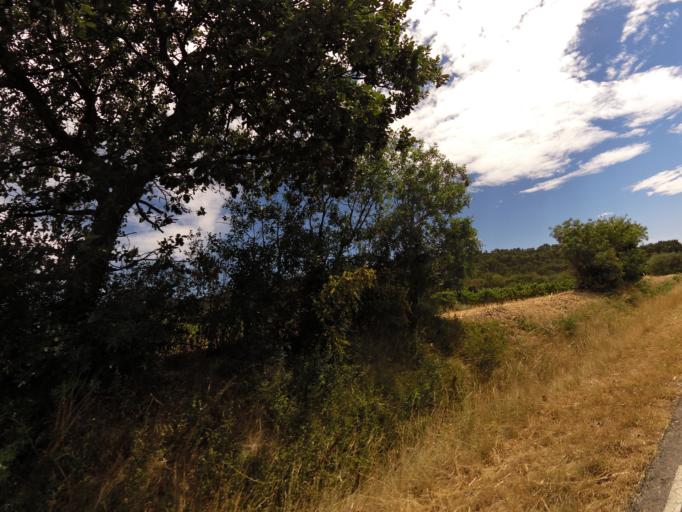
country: FR
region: Languedoc-Roussillon
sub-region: Departement du Gard
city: Quissac
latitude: 43.8480
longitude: 4.0196
